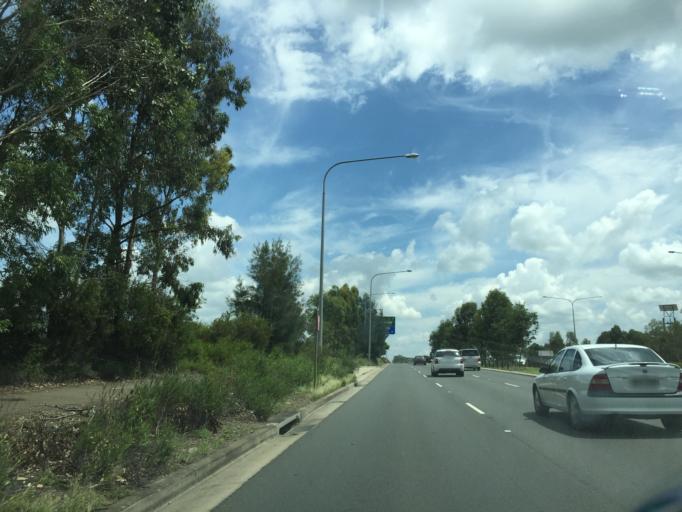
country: AU
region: New South Wales
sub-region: Blacktown
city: Rouse Hill
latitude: -33.6934
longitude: 150.9246
